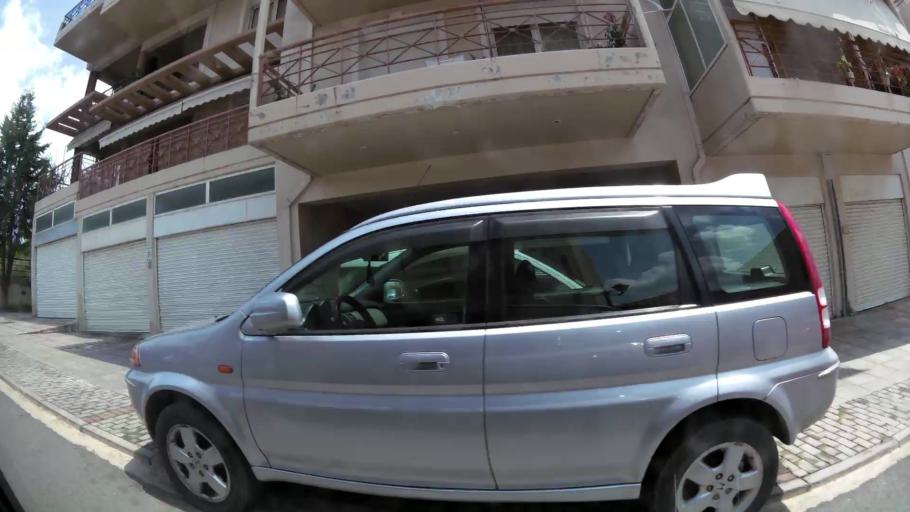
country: GR
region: West Macedonia
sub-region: Nomos Kozanis
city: Kozani
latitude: 40.3086
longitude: 21.7928
